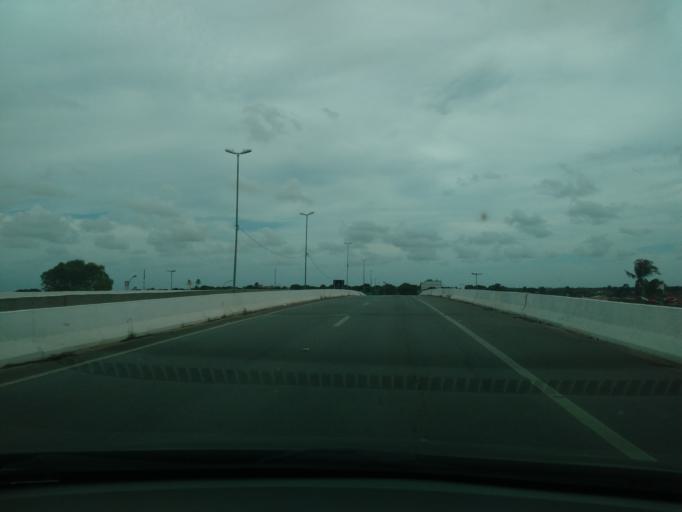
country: BR
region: Alagoas
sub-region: Satuba
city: Satuba
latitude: -9.5136
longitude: -35.8051
